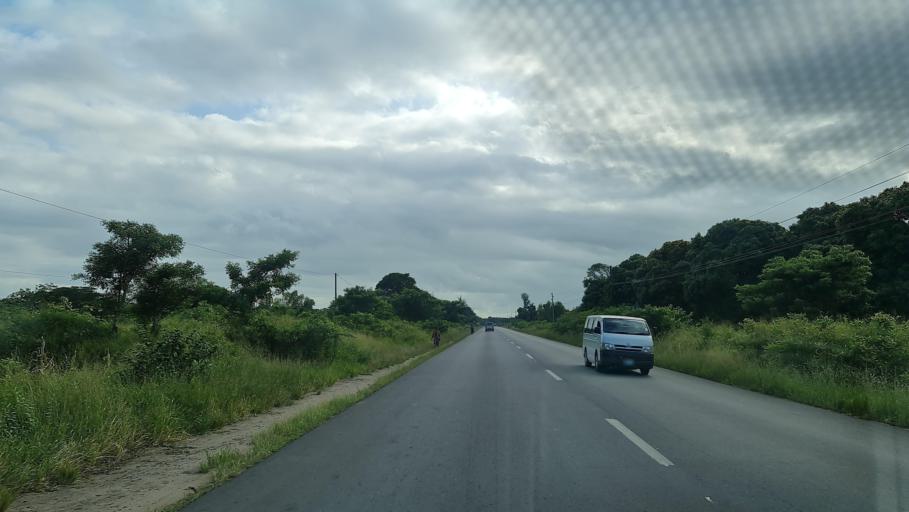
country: MZ
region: Maputo
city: Manhica
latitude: -25.4148
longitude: 32.7377
